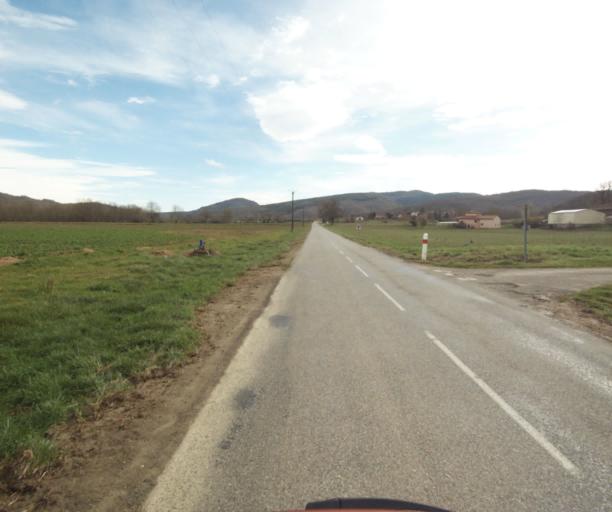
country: FR
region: Midi-Pyrenees
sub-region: Departement de l'Ariege
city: Verniolle
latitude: 43.0622
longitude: 1.7399
